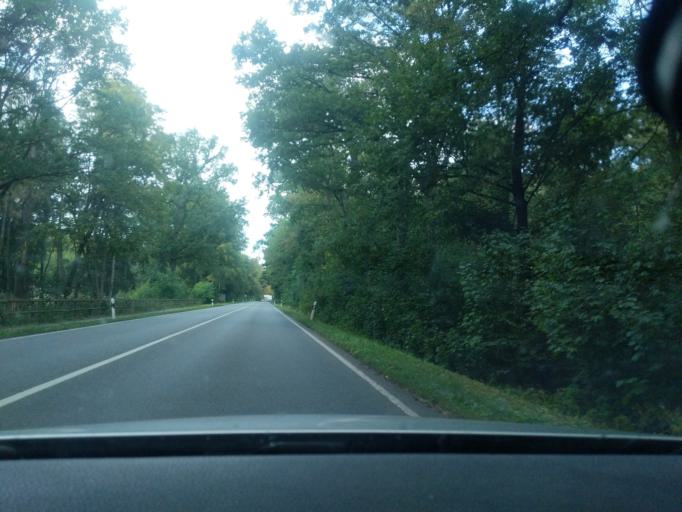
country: DE
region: Lower Saxony
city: Eystrup
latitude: 52.8126
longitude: 9.2007
